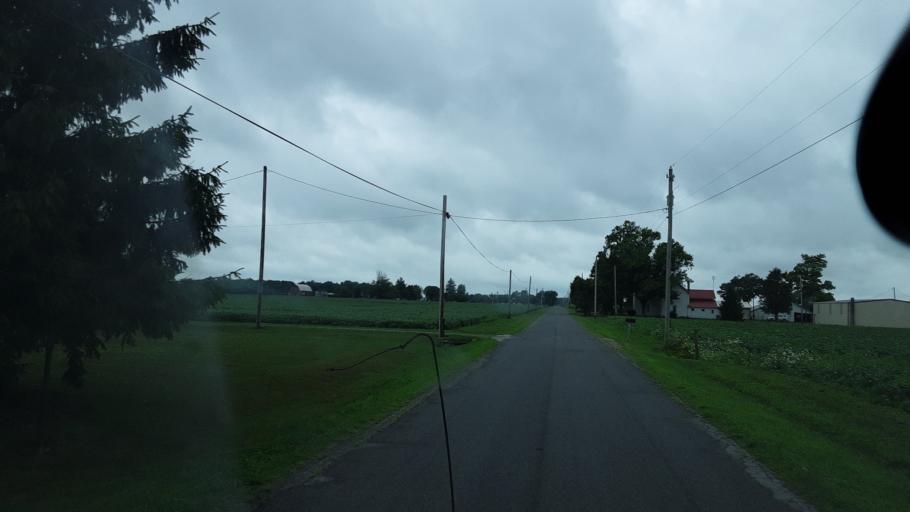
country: US
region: Ohio
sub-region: Van Wert County
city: Convoy
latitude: 40.8224
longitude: -84.7227
